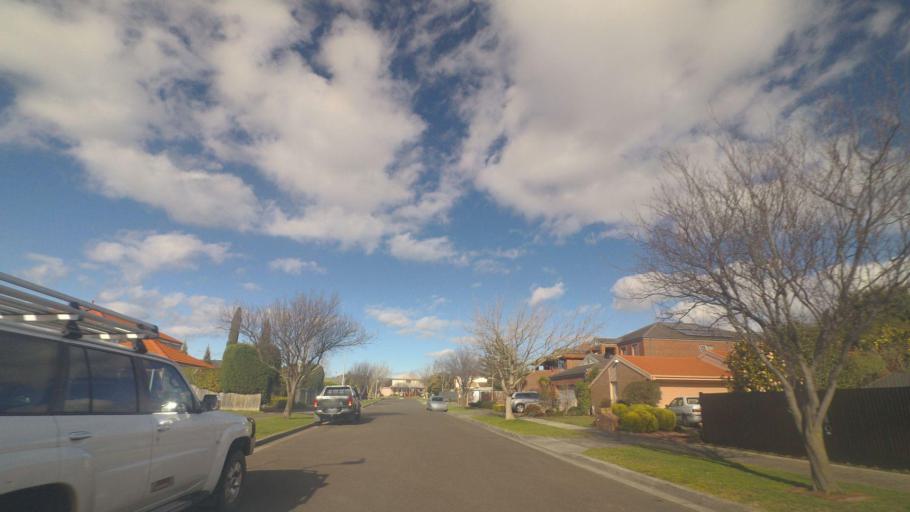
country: AU
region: Victoria
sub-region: Yarra Ranges
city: Lysterfield
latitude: -37.9143
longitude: 145.2794
